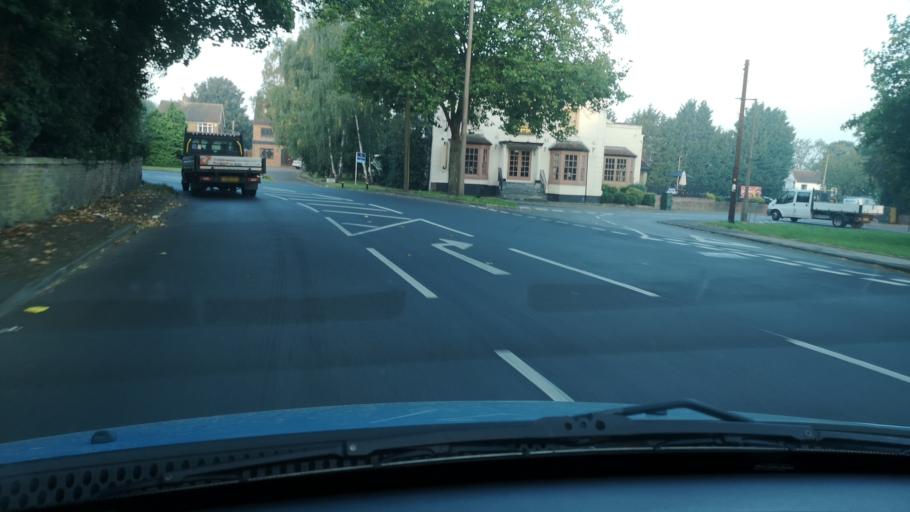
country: GB
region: England
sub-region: Doncaster
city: Hatfield
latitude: 53.5744
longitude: -1.0059
